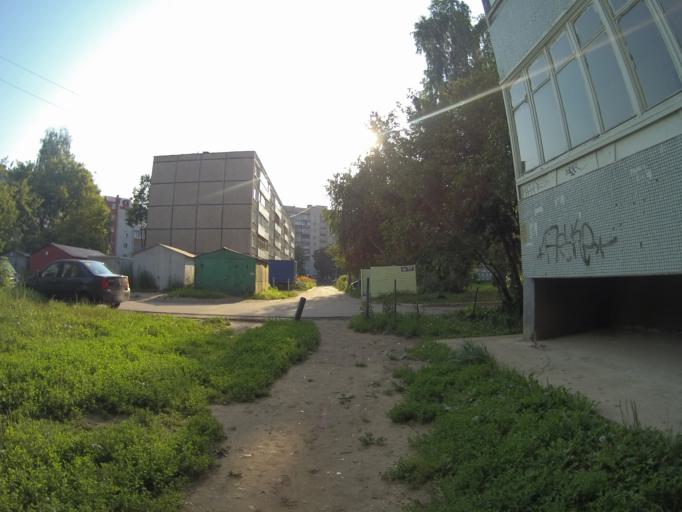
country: RU
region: Vladimir
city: Bogolyubovo
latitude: 56.1728
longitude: 40.4630
